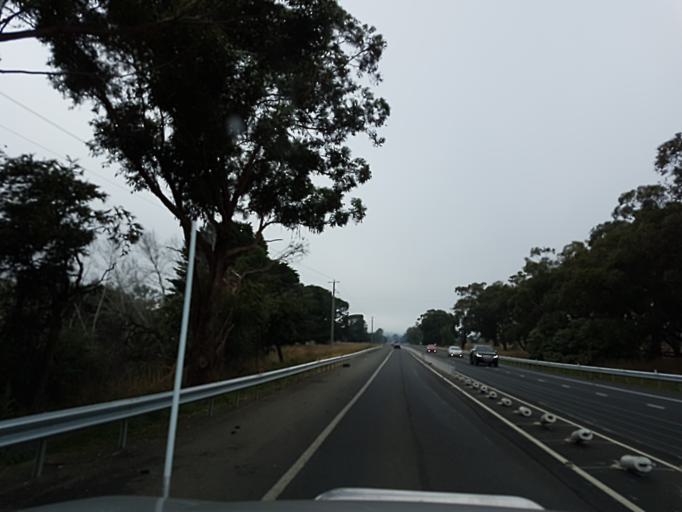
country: AU
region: Victoria
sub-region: Murrindindi
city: Alexandra
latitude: -37.2084
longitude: 145.4564
